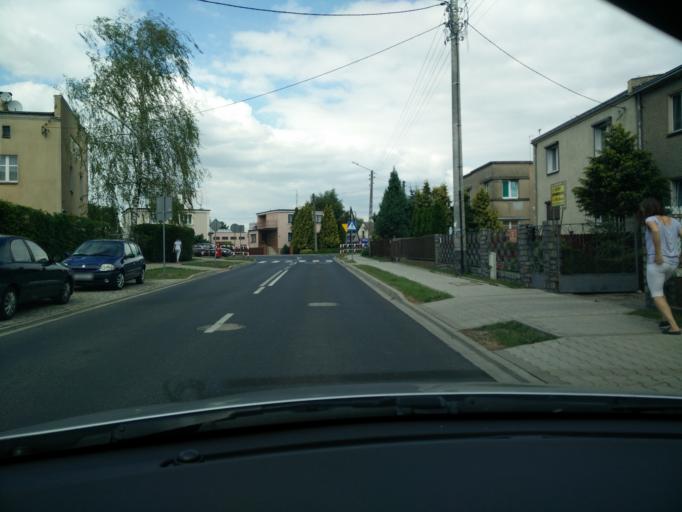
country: PL
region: Greater Poland Voivodeship
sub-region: Powiat sredzki
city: Sroda Wielkopolska
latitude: 52.2296
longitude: 17.2890
